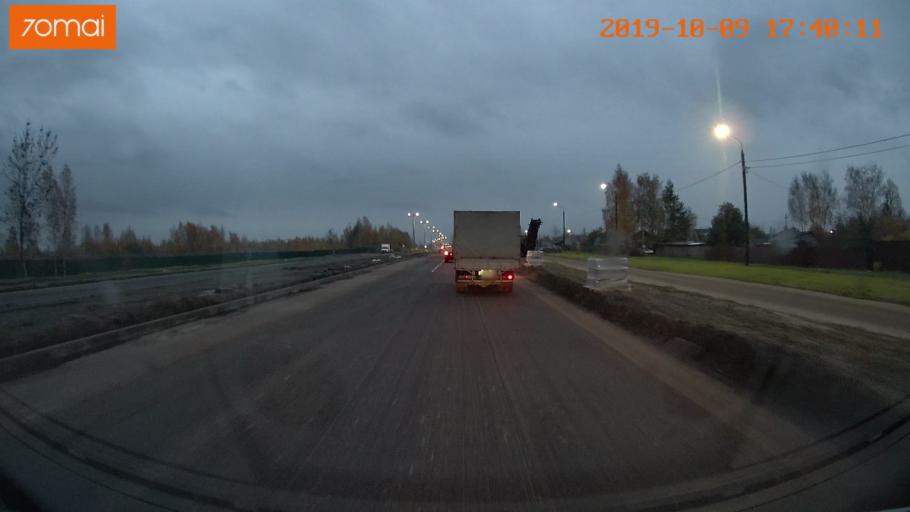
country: RU
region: Ivanovo
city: Bogorodskoye
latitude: 57.0559
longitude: 40.9632
